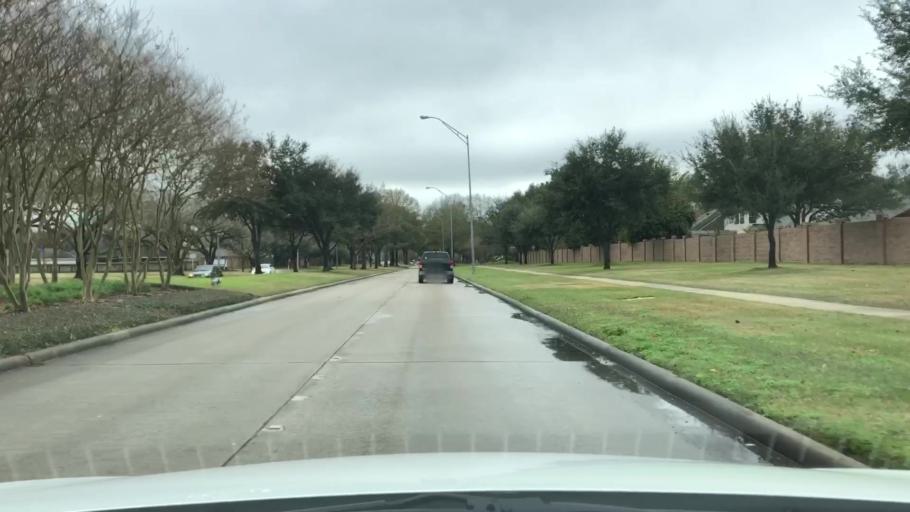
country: US
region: Texas
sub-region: Fort Bend County
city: Cinco Ranch
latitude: 29.7440
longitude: -95.7514
